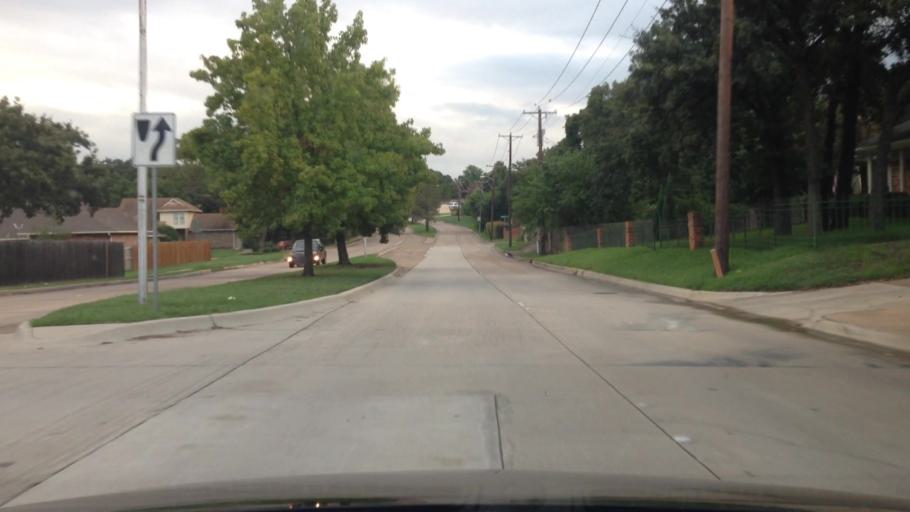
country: US
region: Texas
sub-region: Johnson County
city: Burleson
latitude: 32.5568
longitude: -97.3420
